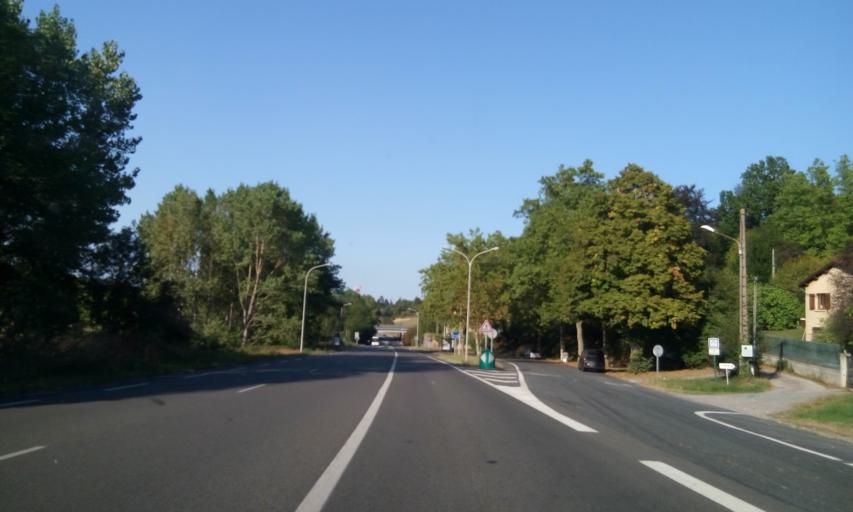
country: FR
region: Rhone-Alpes
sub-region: Departement du Rhone
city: Lissieu
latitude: 45.8568
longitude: 4.7381
